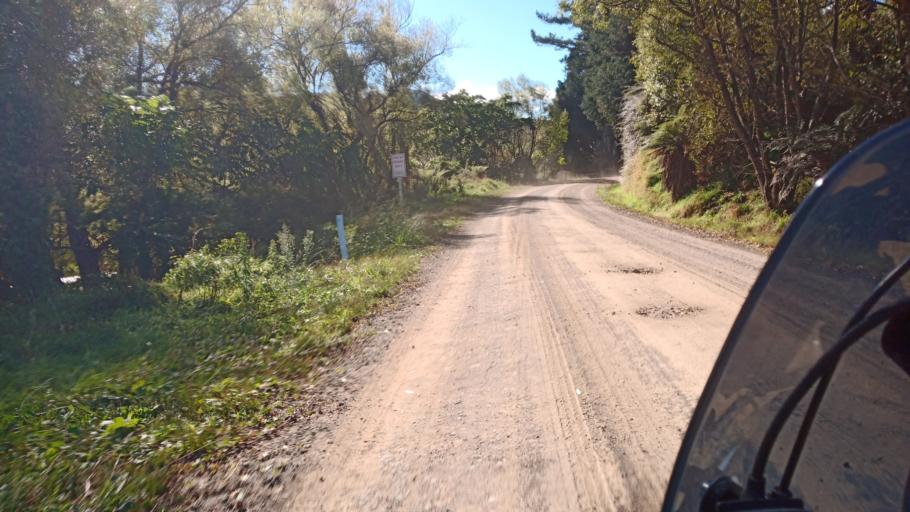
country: NZ
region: Bay of Plenty
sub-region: Opotiki District
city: Opotiki
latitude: -38.2574
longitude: 177.5694
